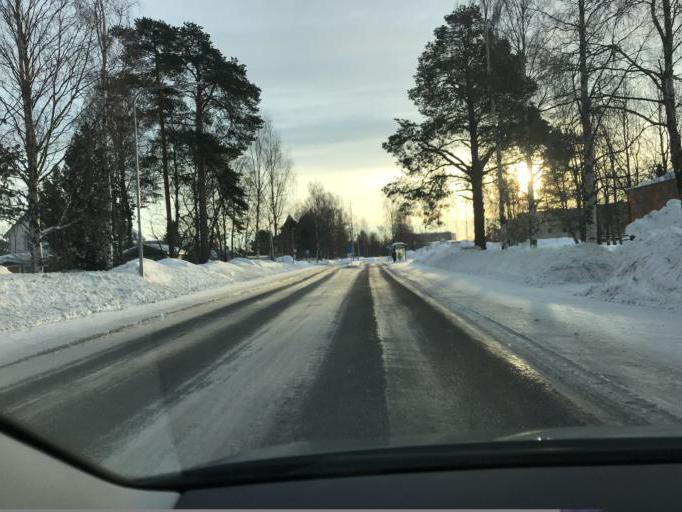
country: SE
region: Norrbotten
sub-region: Lulea Kommun
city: Bergnaset
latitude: 65.6044
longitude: 22.1179
